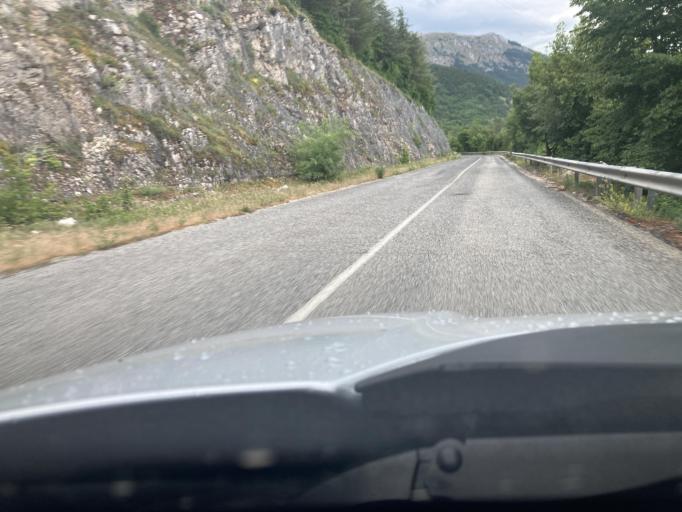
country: IT
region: Abruzzo
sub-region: Provincia dell' Aquila
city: San Panfilo d'Ocre
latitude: 42.2774
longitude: 13.4714
